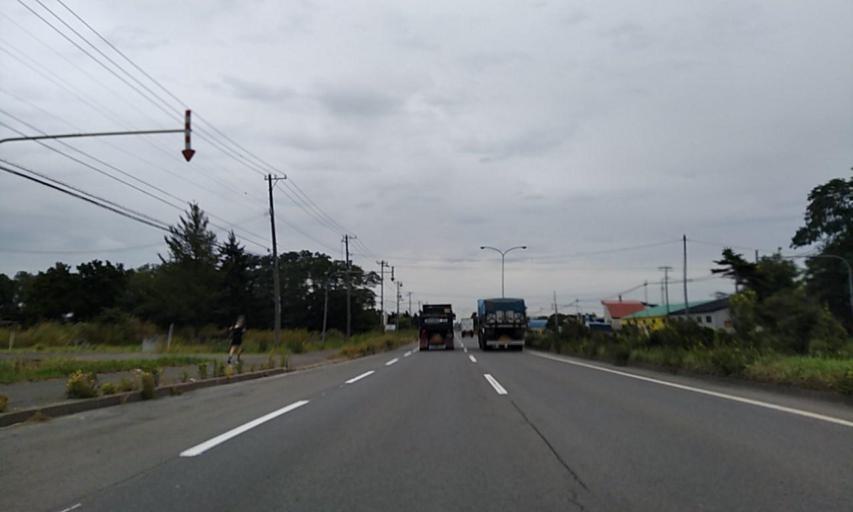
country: JP
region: Hokkaido
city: Sapporo
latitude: 43.1452
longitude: 141.2109
